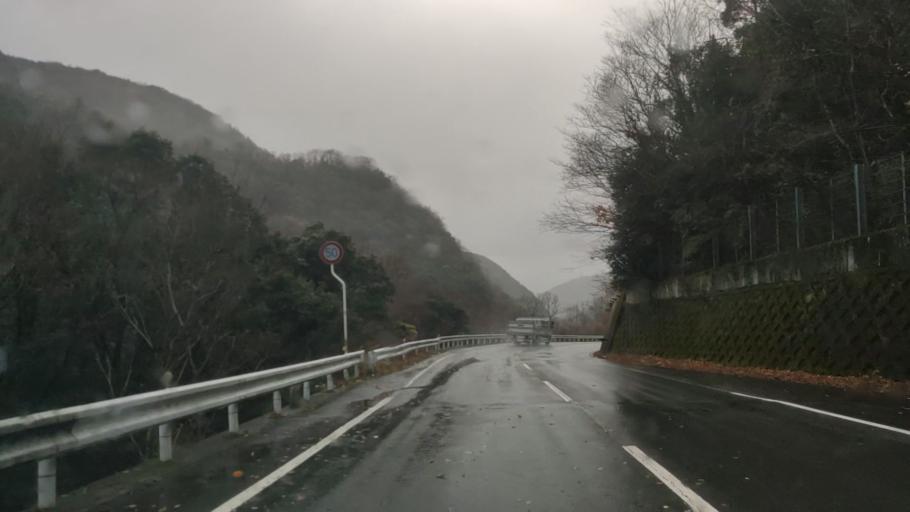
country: JP
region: Tokushima
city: Kamojimacho-jogejima
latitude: 34.1450
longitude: 134.3539
